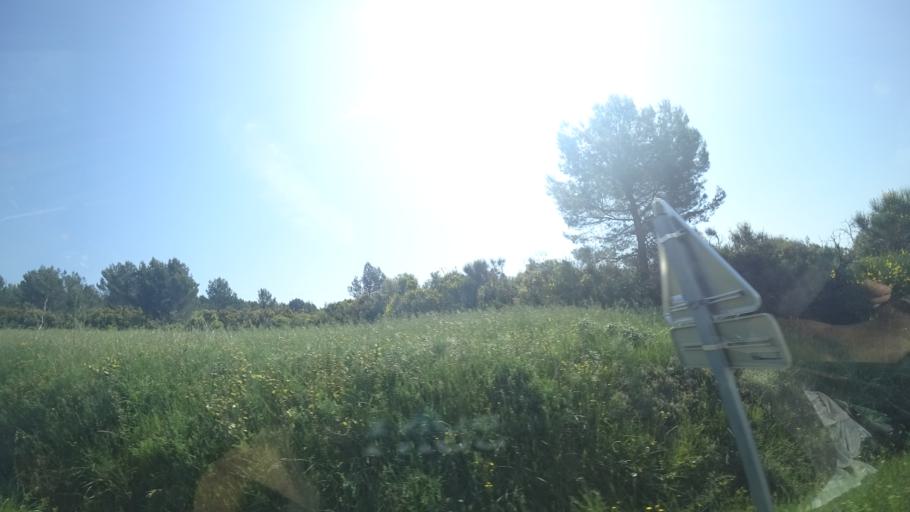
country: FR
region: Languedoc-Roussillon
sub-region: Departement de l'Herault
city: Olonzac
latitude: 43.3373
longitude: 2.7329
